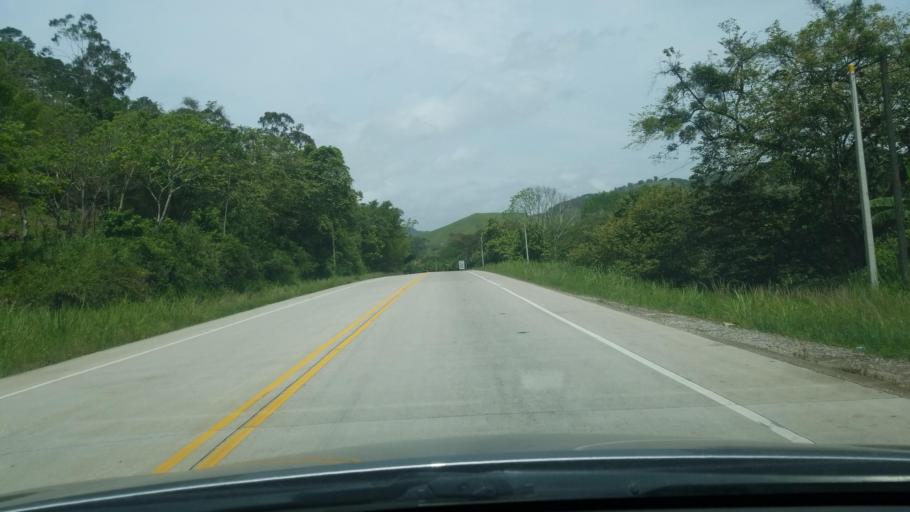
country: HN
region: Copan
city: Agua Caliente
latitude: 14.8595
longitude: -88.7940
